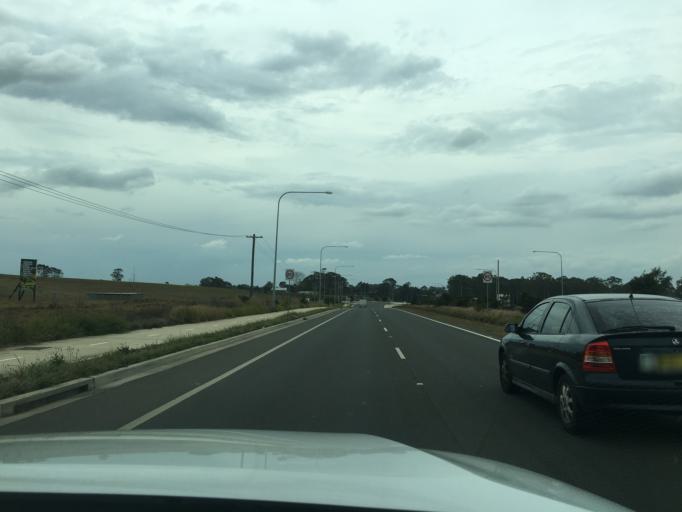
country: AU
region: New South Wales
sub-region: Campbelltown Municipality
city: Denham Court
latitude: -33.9846
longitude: 150.7960
